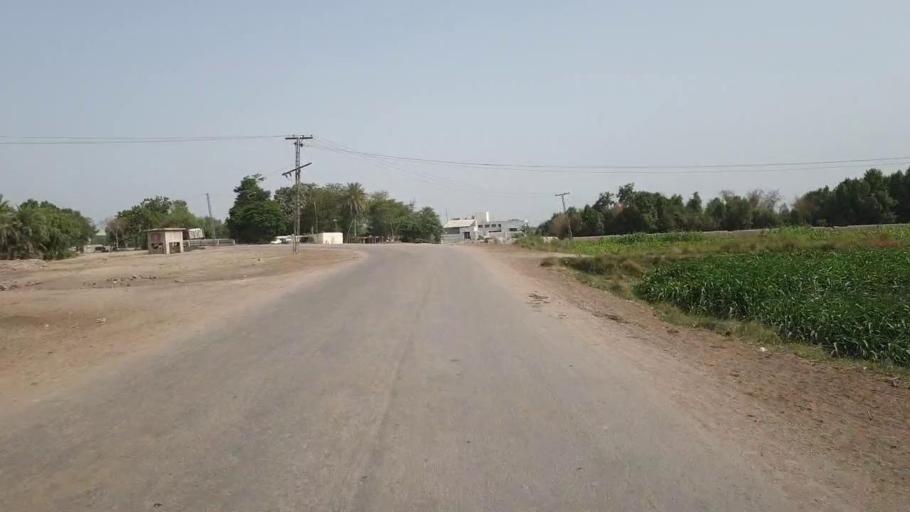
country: PK
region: Sindh
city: Daulatpur
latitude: 26.5600
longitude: 67.9819
